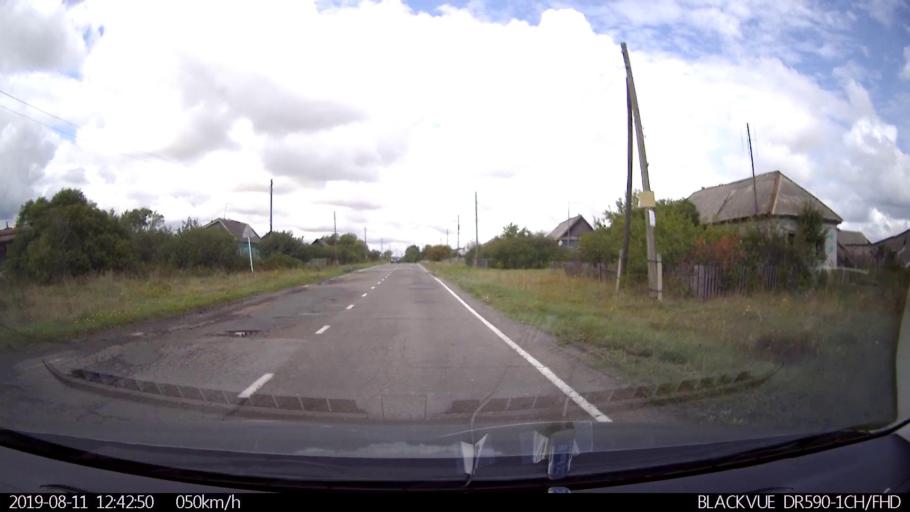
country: RU
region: Ulyanovsk
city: Ignatovka
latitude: 53.8484
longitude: 47.7473
